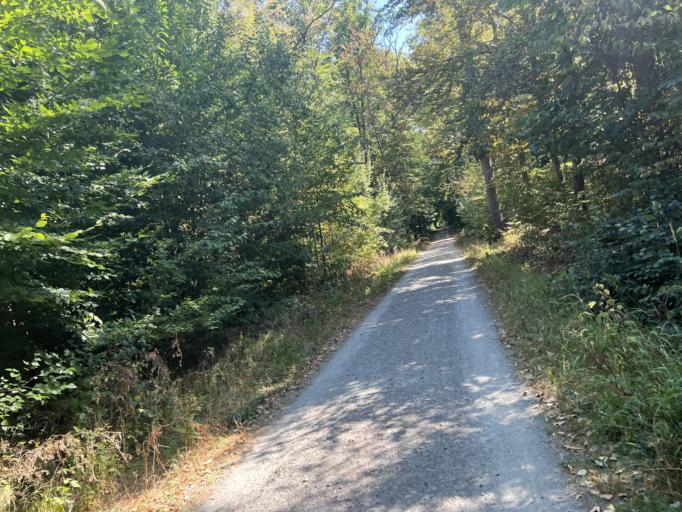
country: DE
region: Hesse
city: Heusenstamm
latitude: 50.0805
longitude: 8.7894
